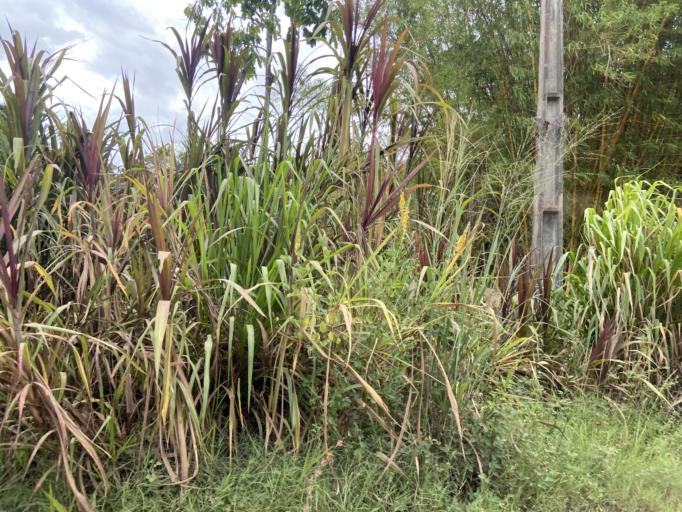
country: BR
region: Para
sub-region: Maraba
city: Maraba
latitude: -5.2612
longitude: -48.9943
